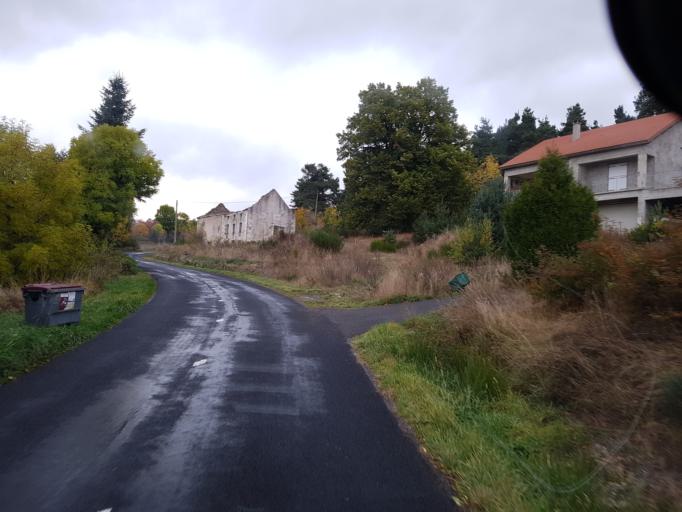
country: FR
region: Languedoc-Roussillon
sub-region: Departement de la Lozere
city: Langogne
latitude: 44.7142
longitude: 3.7975
